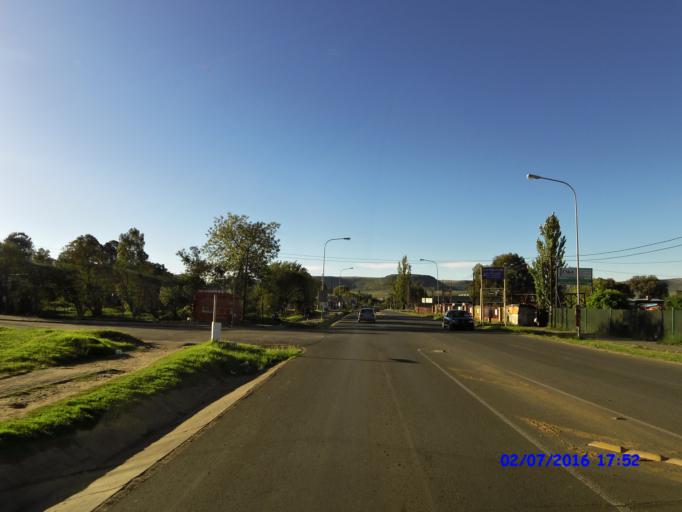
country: LS
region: Maseru
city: Maseru
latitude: -29.3085
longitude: 27.4860
